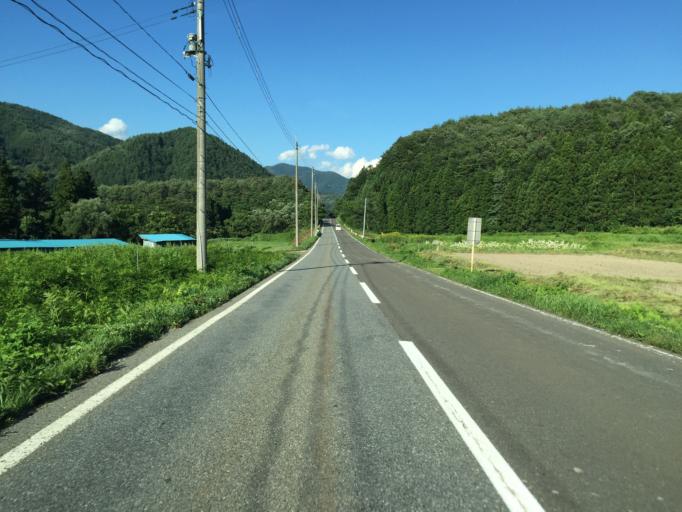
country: JP
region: Yamagata
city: Kaminoyama
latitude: 38.0118
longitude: 140.3826
